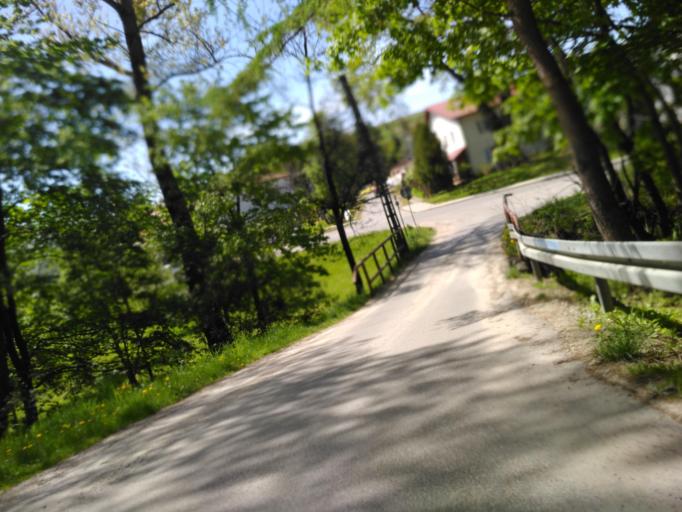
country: PL
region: Subcarpathian Voivodeship
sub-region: Powiat krosnienski
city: Iwonicz-Zdroj
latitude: 49.5438
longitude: 21.7612
